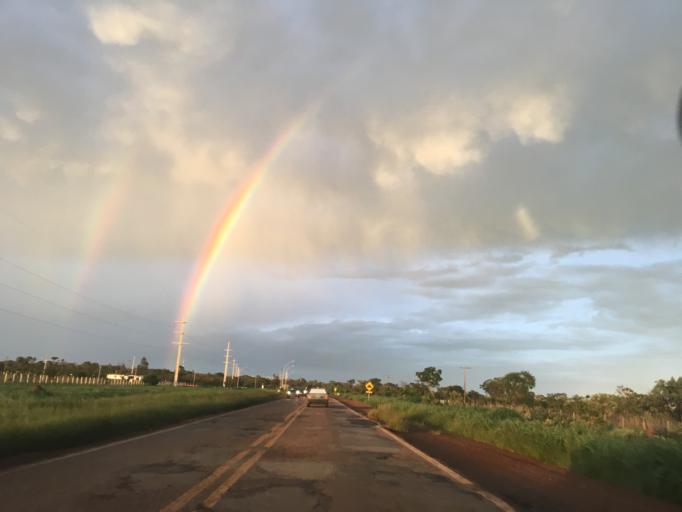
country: BR
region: Federal District
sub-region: Brasilia
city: Brasilia
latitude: -15.9744
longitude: -47.9758
